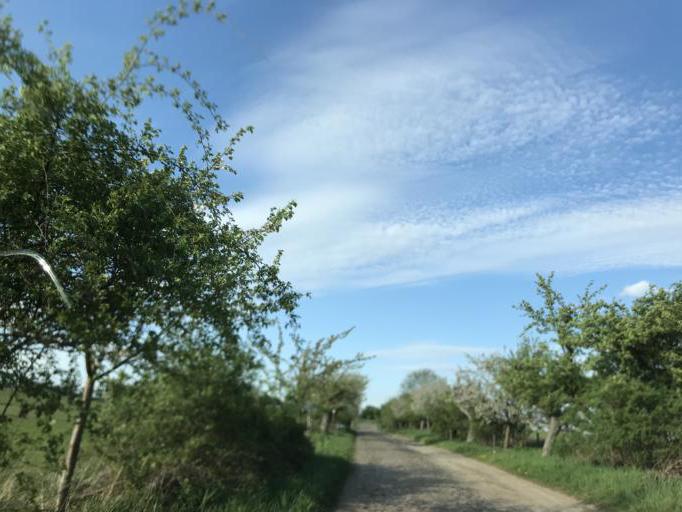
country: DE
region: Brandenburg
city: Joachimsthal
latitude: 52.9740
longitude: 13.7259
